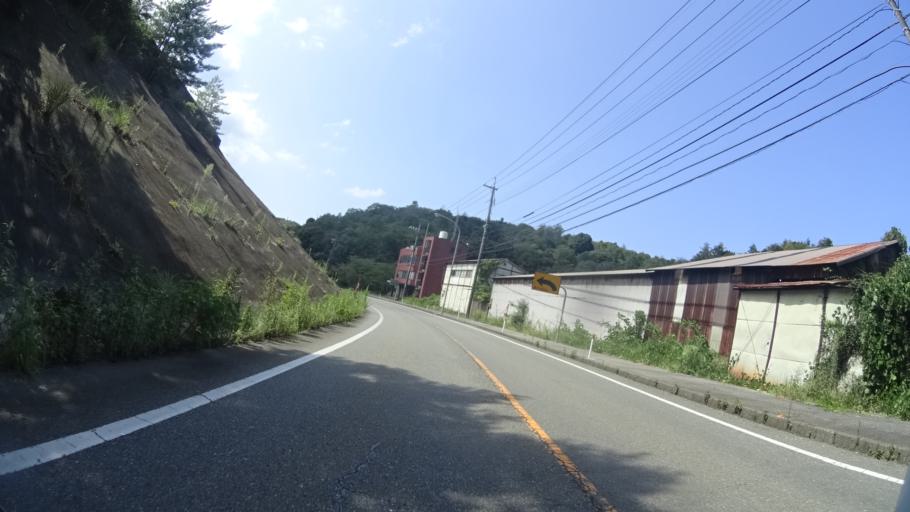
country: JP
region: Shimane
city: Masuda
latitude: 34.6259
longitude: 131.6145
